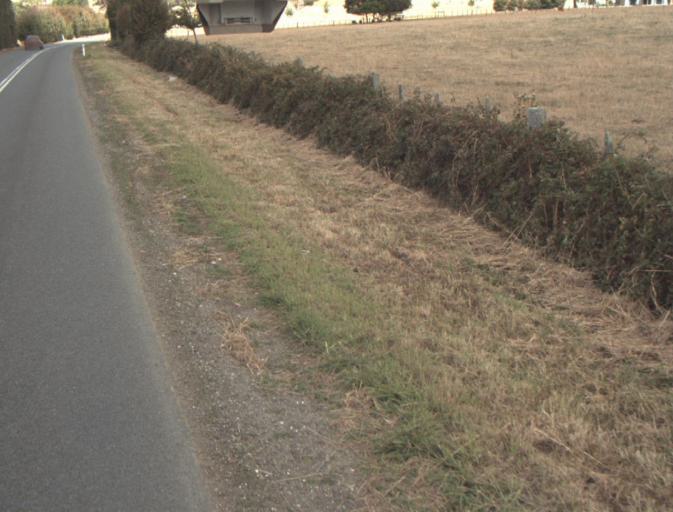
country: AU
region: Tasmania
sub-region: Launceston
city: Mayfield
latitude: -41.2292
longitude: 147.1232
